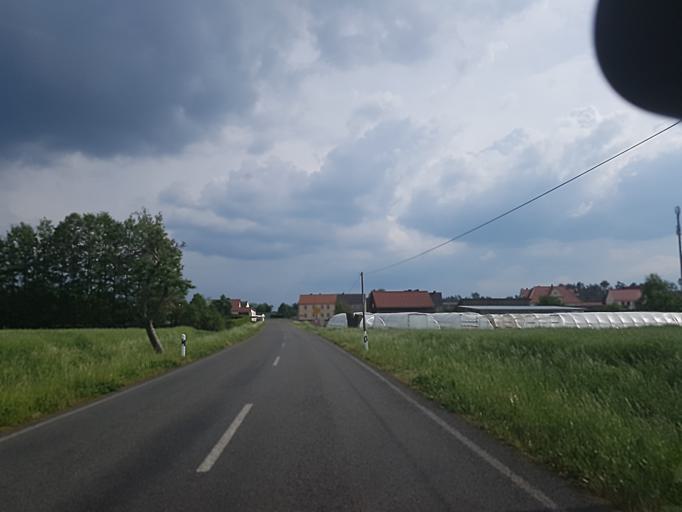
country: DE
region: Saxony-Anhalt
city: Rodleben
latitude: 51.9880
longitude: 12.2334
